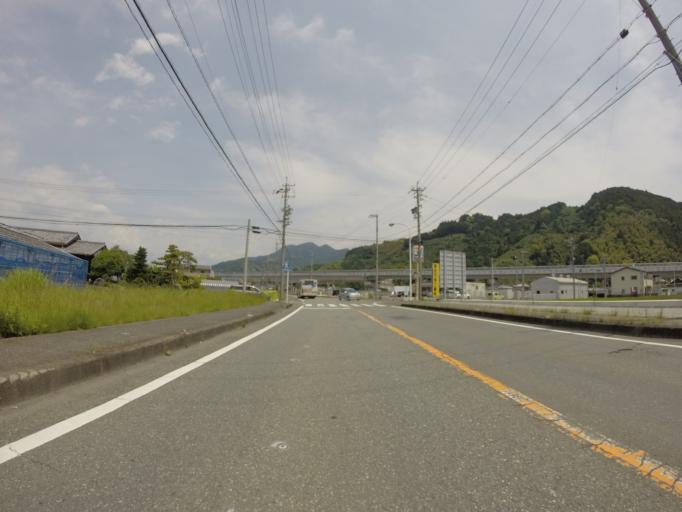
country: JP
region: Shizuoka
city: Shizuoka-shi
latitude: 35.0291
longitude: 138.3789
